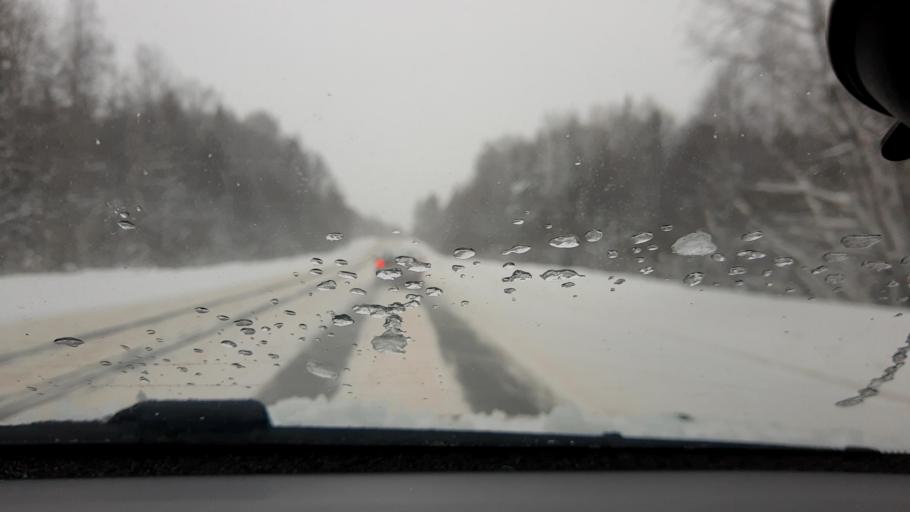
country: RU
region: Nizjnij Novgorod
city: Purekh
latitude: 56.6357
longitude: 43.1255
